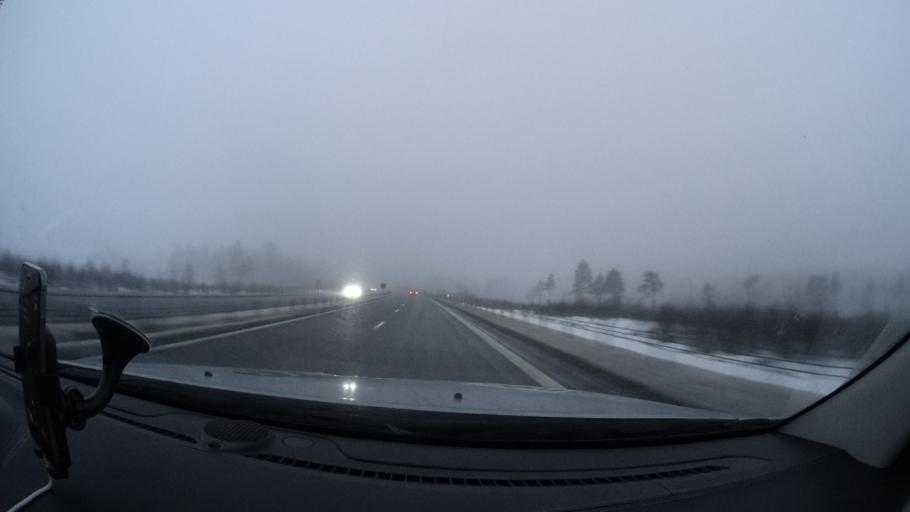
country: SE
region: Kronoberg
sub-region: Markaryds Kommun
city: Markaryd
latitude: 56.3822
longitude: 13.5061
